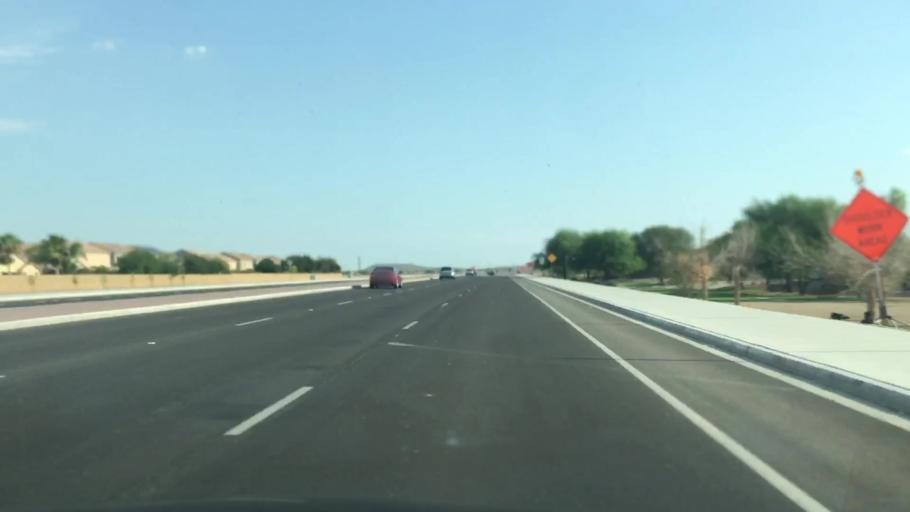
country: US
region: Arizona
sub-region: Pinal County
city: San Tan Valley
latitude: 33.1579
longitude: -111.5448
